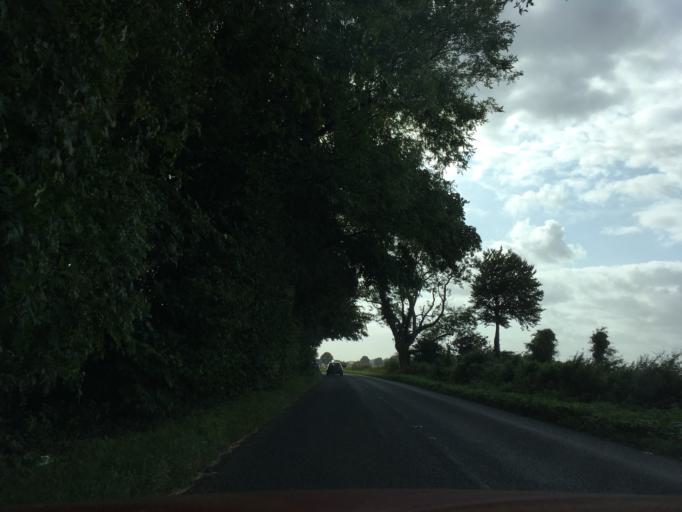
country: GB
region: England
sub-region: Gloucestershire
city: Dursley
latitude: 51.6689
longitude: -2.2914
